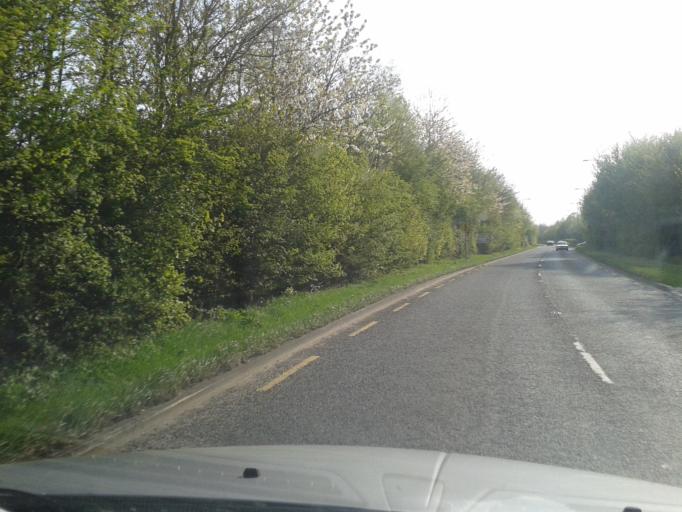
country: IE
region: Leinster
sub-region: Dublin City
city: Finglas
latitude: 53.4301
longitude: -6.2992
